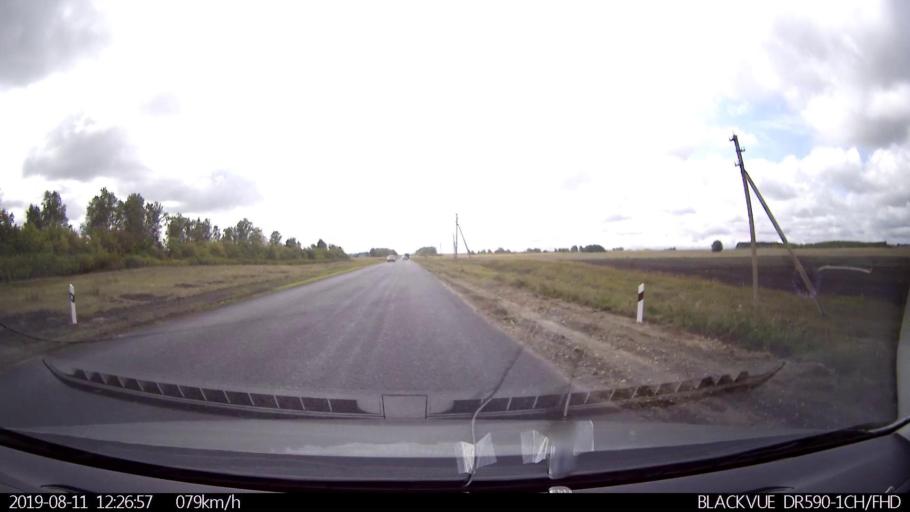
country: RU
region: Ulyanovsk
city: Ignatovka
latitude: 53.8598
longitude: 47.9269
